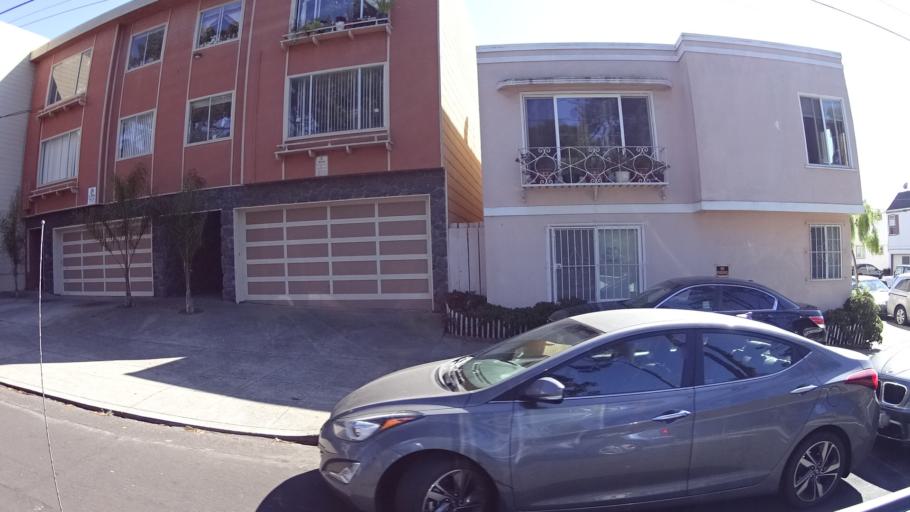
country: US
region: California
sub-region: San Mateo County
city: Daly City
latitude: 37.7009
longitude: -122.4678
